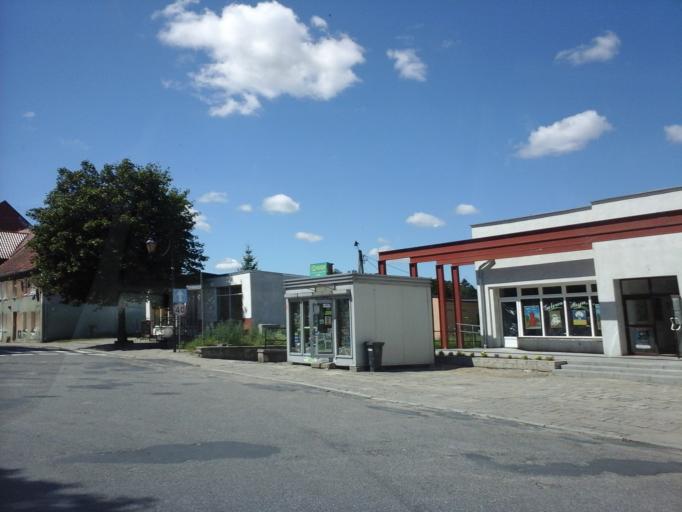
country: PL
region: West Pomeranian Voivodeship
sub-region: Powiat choszczenski
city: Recz
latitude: 53.2603
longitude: 15.5460
